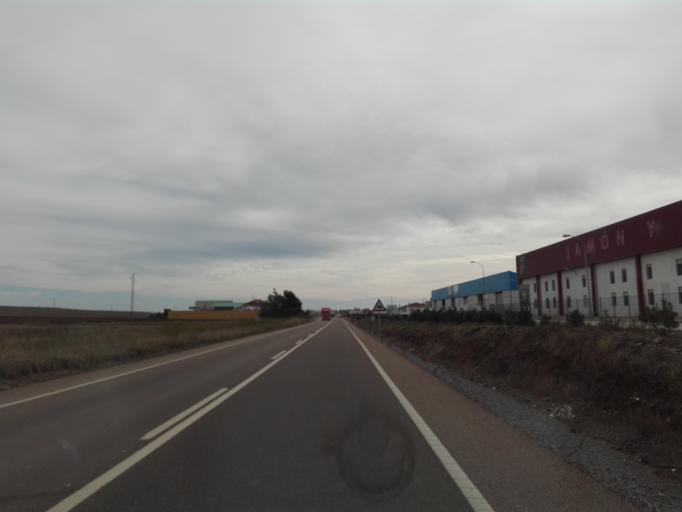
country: ES
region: Extremadura
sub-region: Provincia de Badajoz
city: Llerena
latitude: 38.2547
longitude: -6.0307
